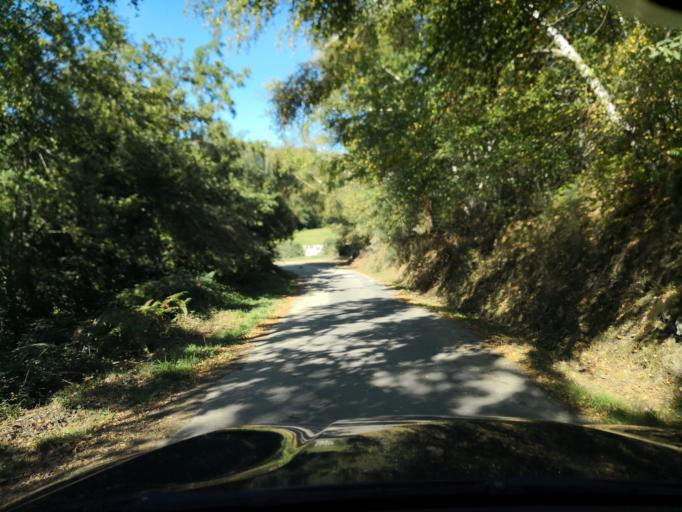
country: PT
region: Vila Real
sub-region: Santa Marta de Penaguiao
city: Santa Marta de Penaguiao
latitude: 41.3007
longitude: -7.8656
